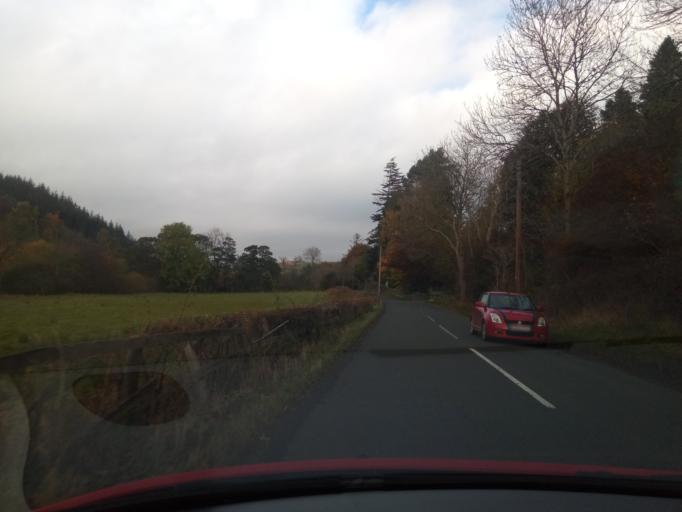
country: GB
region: Scotland
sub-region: The Scottish Borders
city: Selkirk
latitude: 55.6020
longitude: -2.8711
